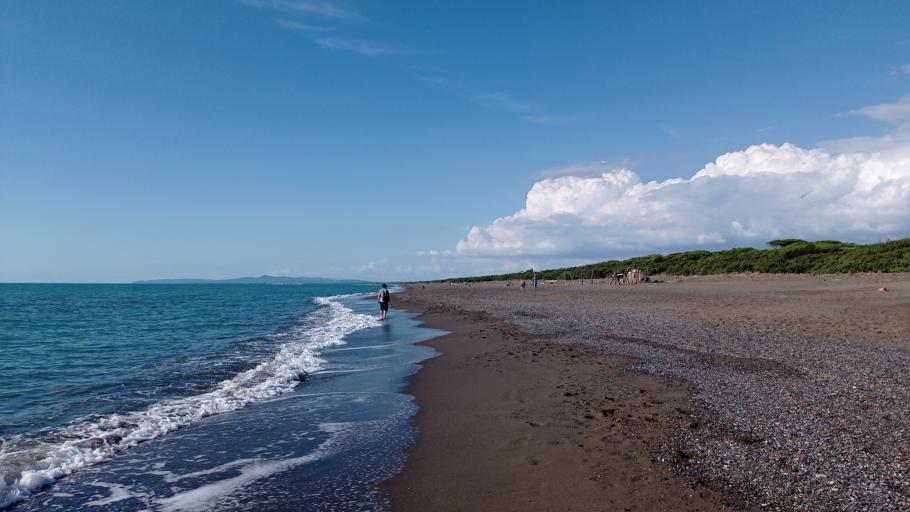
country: IT
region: Tuscany
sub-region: Provincia di Livorno
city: Donoratico
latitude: 43.1963
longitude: 10.5351
